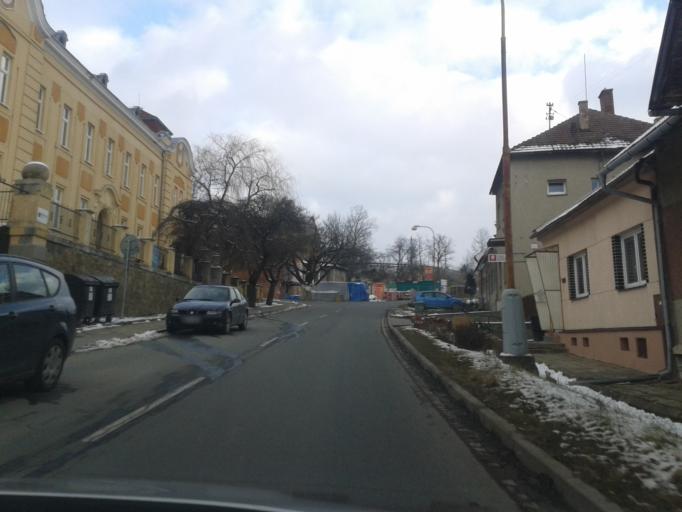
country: CZ
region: Olomoucky
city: Konice
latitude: 49.5929
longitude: 16.8894
